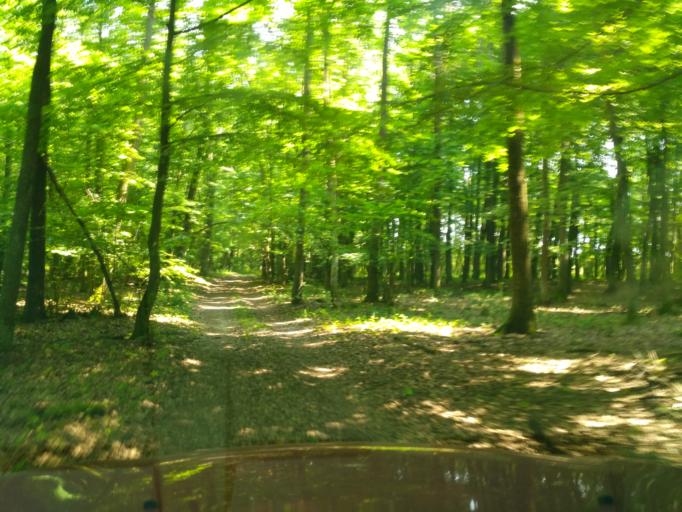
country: SK
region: Kosicky
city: Moldava nad Bodvou
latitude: 48.6210
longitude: 21.0457
